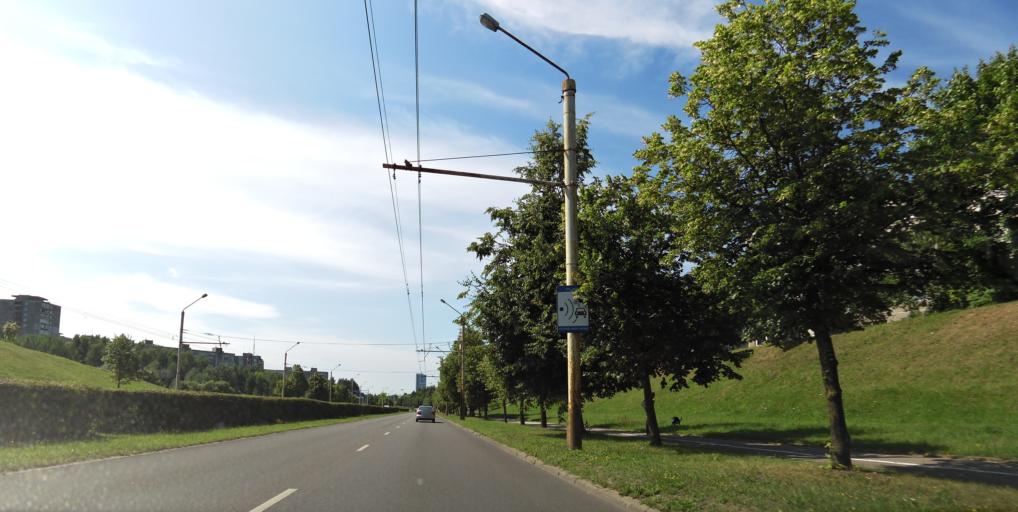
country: LT
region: Vilnius County
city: Justiniskes
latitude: 54.7135
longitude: 25.2187
